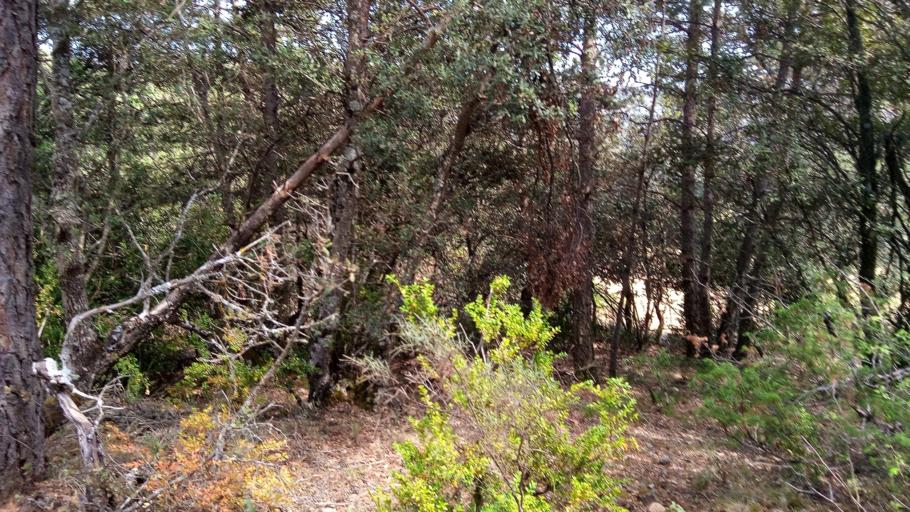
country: ES
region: Aragon
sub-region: Provincia de Huesca
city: Lascuarre
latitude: 42.2842
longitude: 0.4937
